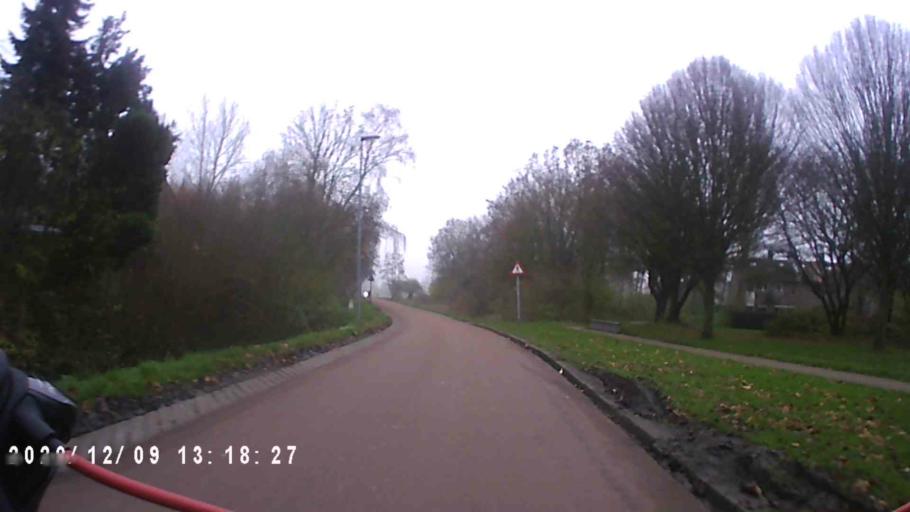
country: NL
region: Groningen
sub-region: Gemeente Groningen
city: Oosterpark
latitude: 53.2534
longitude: 6.5920
